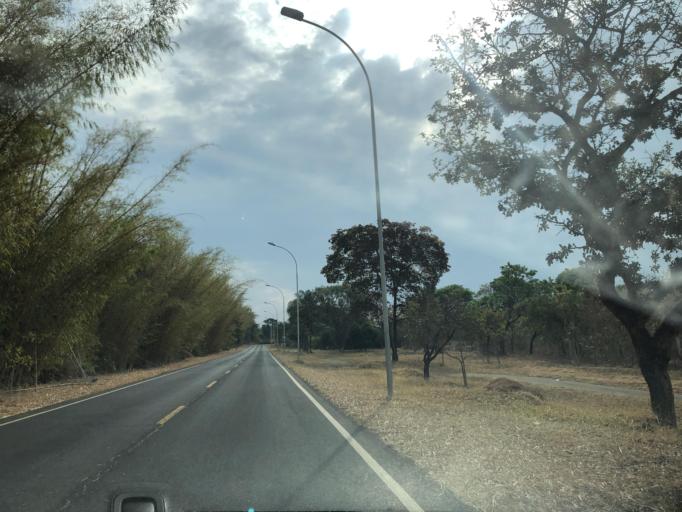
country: BR
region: Federal District
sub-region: Brasilia
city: Brasilia
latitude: -15.9439
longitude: -47.9836
